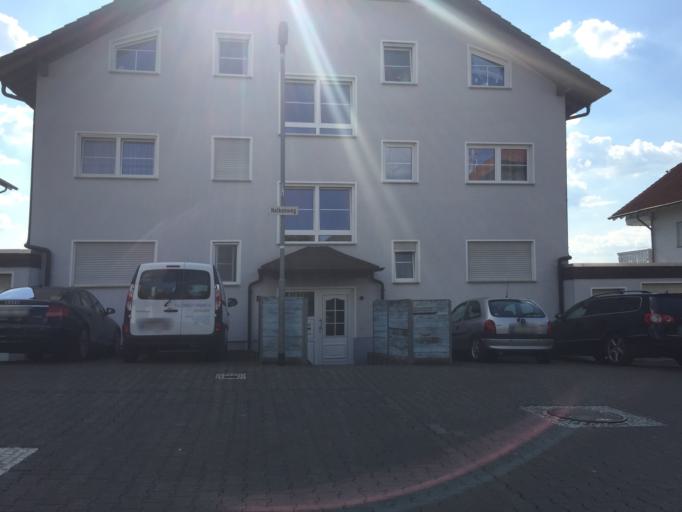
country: DE
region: Hesse
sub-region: Regierungsbezirk Giessen
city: Langgons
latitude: 50.5337
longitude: 8.7024
